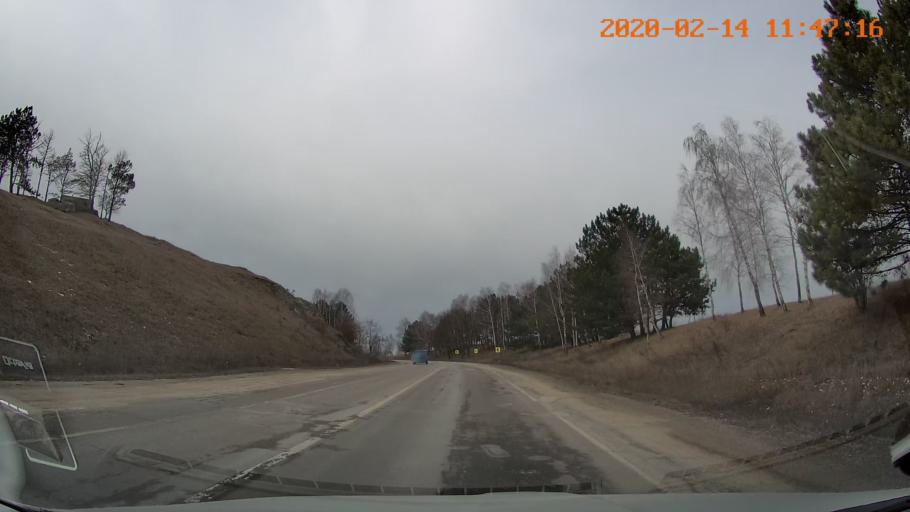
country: MD
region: Briceni
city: Briceni
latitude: 48.3167
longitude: 26.9734
